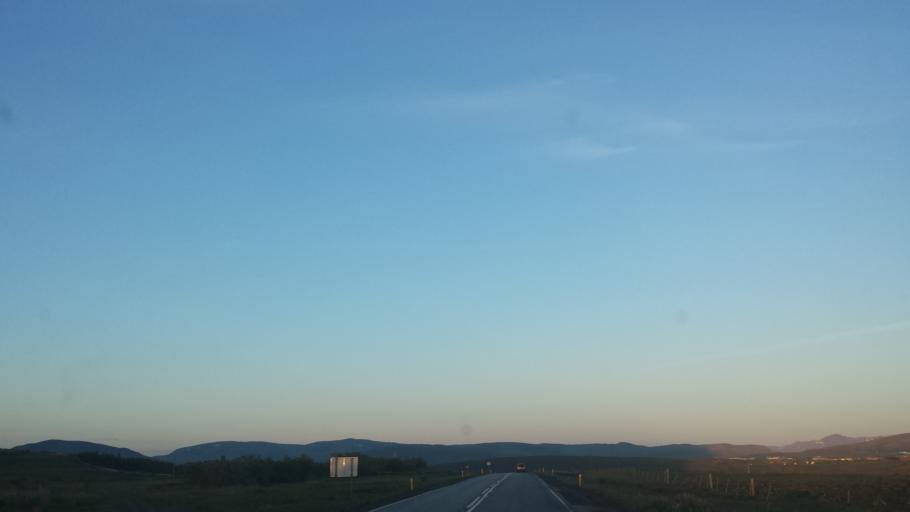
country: IS
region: Capital Region
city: Mosfellsbaer
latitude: 64.2094
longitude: -21.7652
